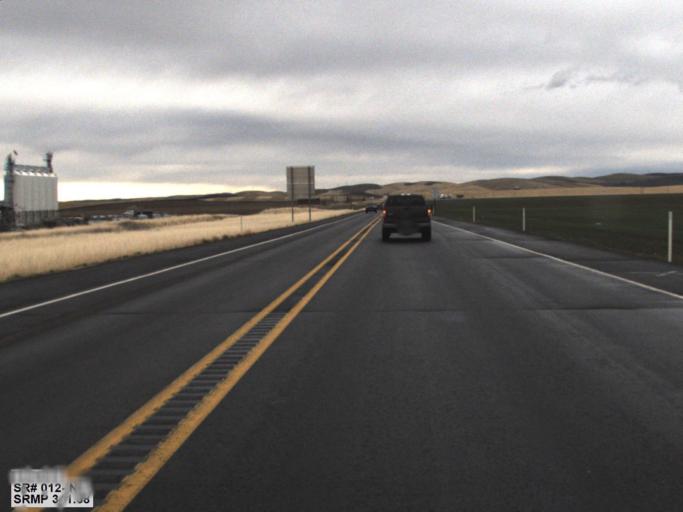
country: US
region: Washington
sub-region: Walla Walla County
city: Walla Walla East
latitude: 46.0916
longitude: -118.2571
